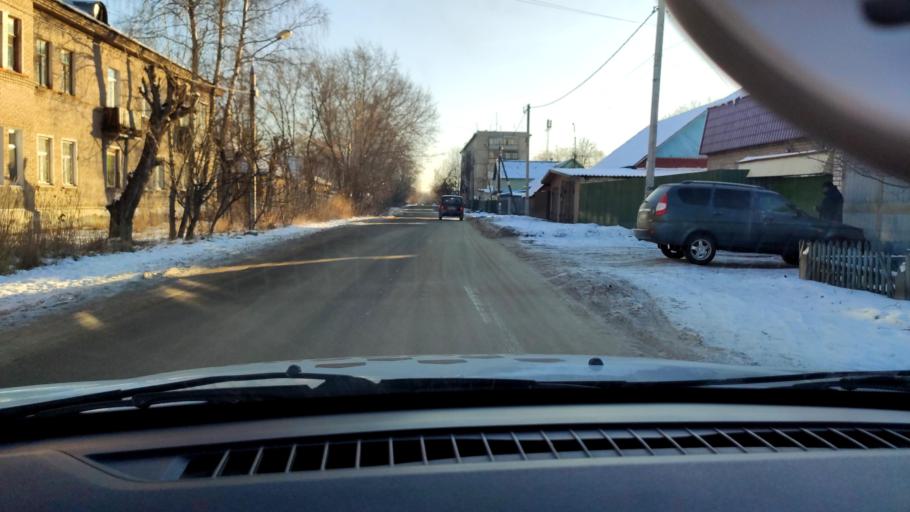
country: RU
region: Perm
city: Overyata
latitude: 58.0073
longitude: 55.9175
